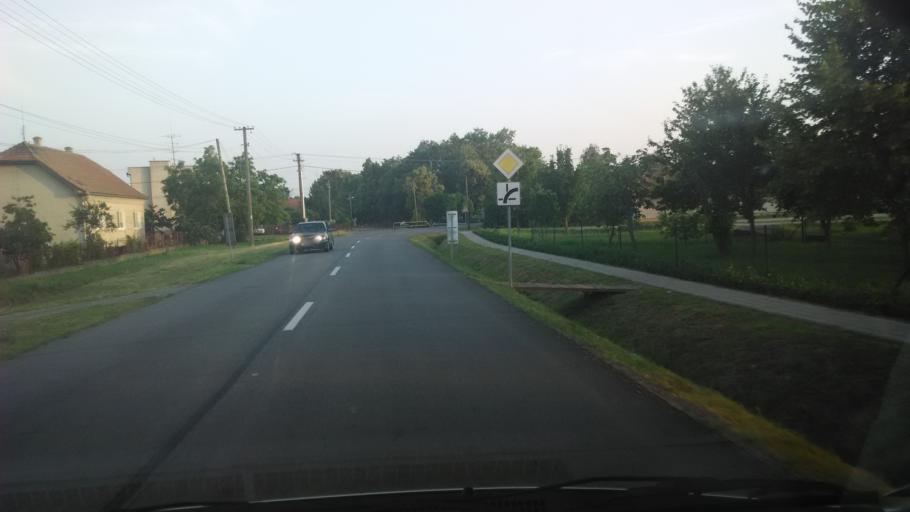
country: SK
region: Nitriansky
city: Tlmace
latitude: 48.1579
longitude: 18.4505
